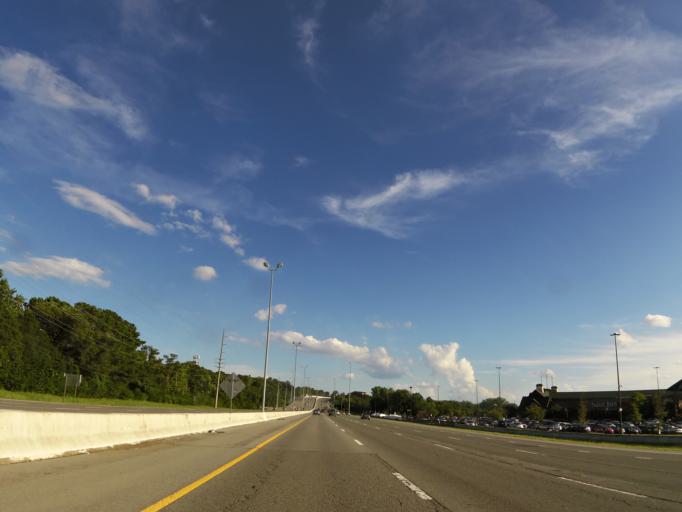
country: US
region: Tennessee
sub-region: Davidson County
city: Lakewood
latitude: 36.2033
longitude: -86.6895
